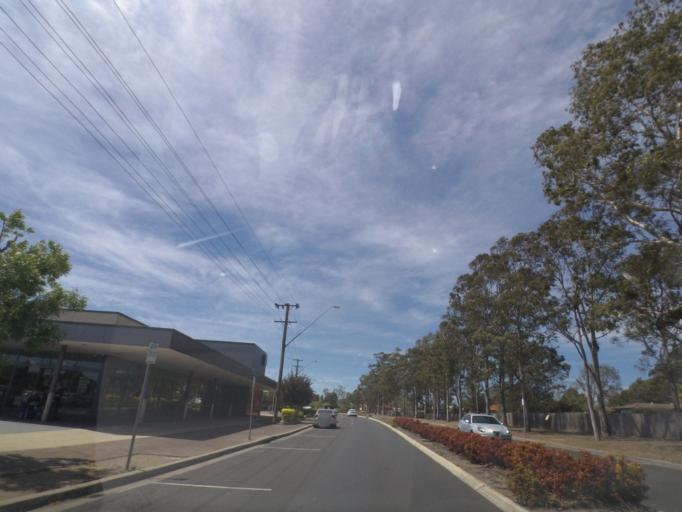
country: AU
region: New South Wales
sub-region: Wollondilly
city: Picton
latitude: -34.2258
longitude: 150.5919
